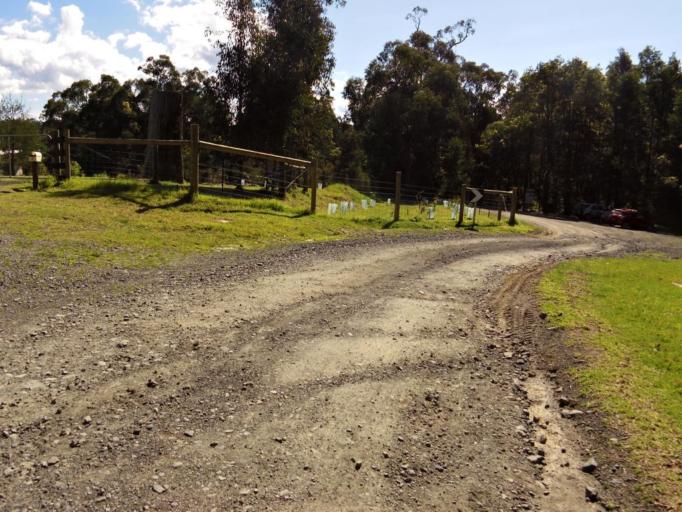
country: AU
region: Victoria
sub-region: Baw Baw
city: Warragul
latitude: -38.0701
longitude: 145.9300
